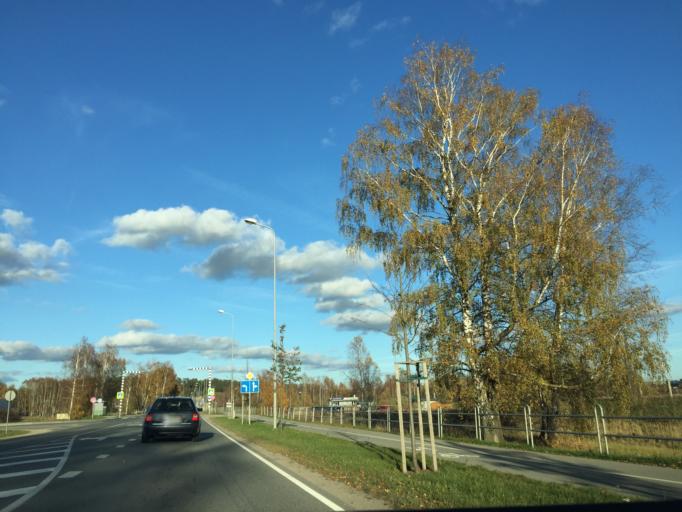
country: LV
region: Tukuma Rajons
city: Tukums
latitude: 56.9551
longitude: 23.1199
